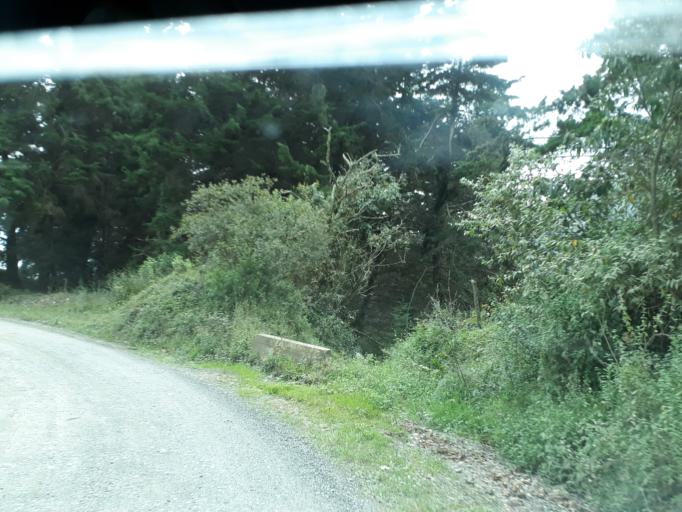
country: CO
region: Cundinamarca
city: Pacho
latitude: 5.2310
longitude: -74.1882
